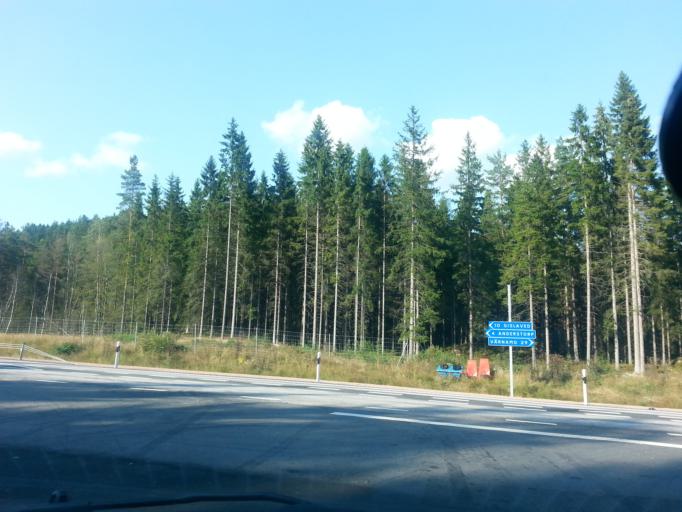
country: SE
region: Joenkoeping
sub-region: Gislaveds Kommun
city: Reftele
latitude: 57.2435
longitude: 13.6458
